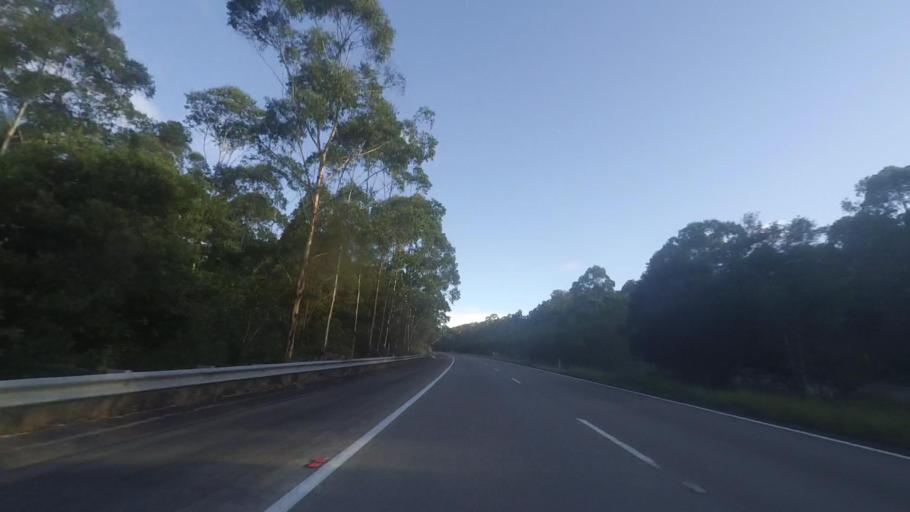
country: AU
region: New South Wales
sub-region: Great Lakes
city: Bulahdelah
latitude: -32.2755
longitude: 152.3294
